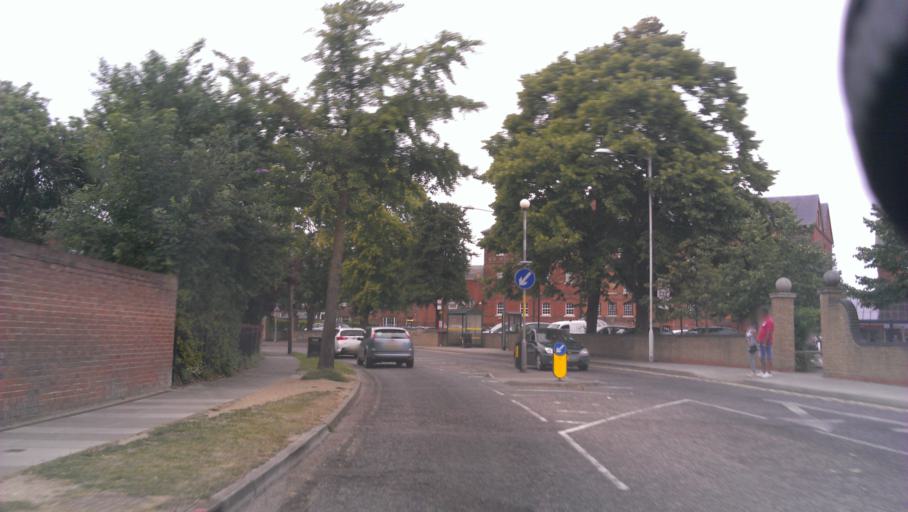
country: GB
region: England
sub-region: Kent
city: Faversham
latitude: 51.3159
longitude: 0.8930
